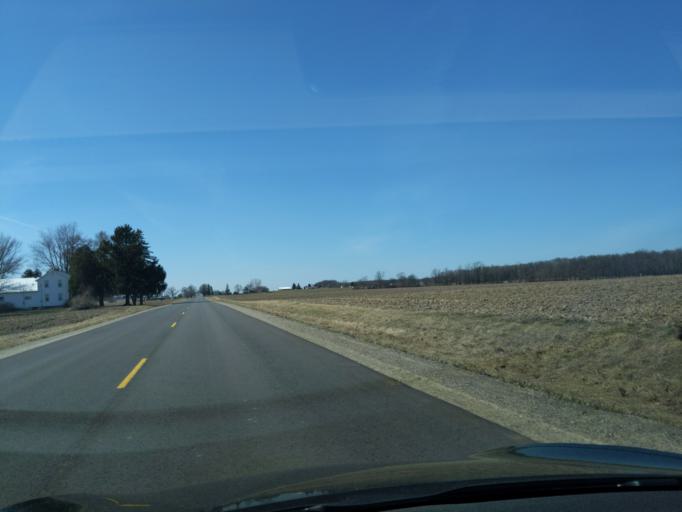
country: US
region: Michigan
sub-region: Eaton County
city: Grand Ledge
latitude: 42.7266
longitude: -84.8818
